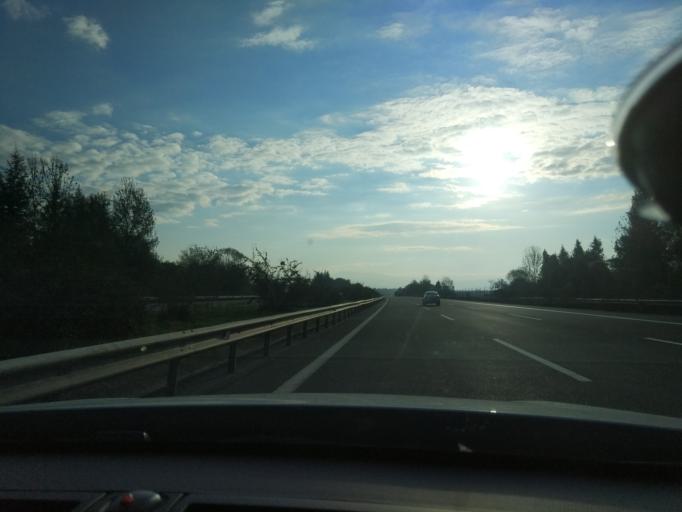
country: TR
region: Duzce
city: Duzce
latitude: 40.8047
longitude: 31.1601
